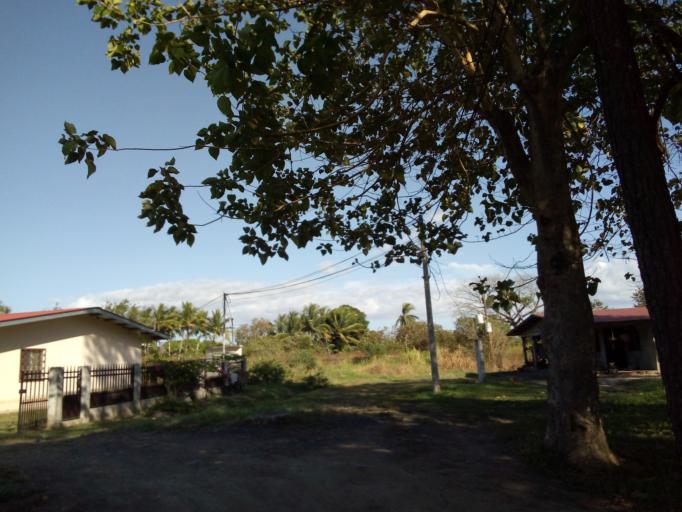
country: PA
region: Veraguas
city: Santiago de Veraguas
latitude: 8.1079
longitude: -80.9677
